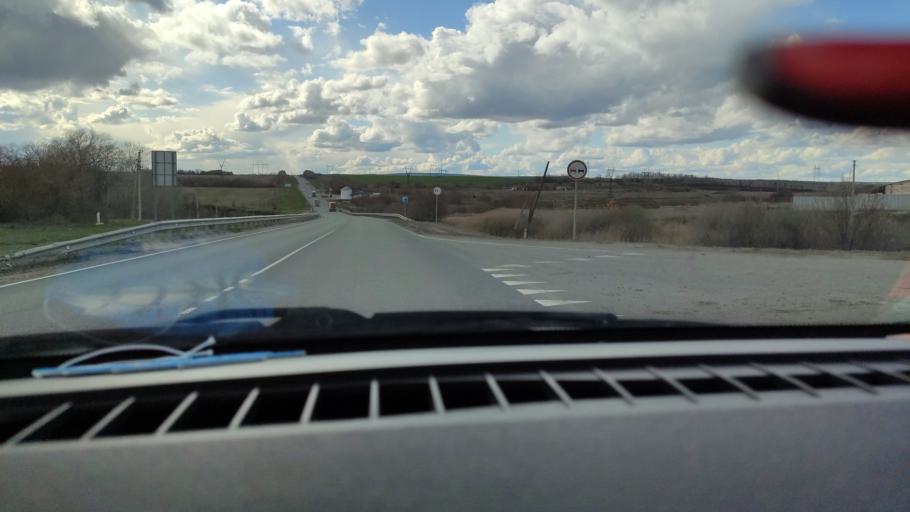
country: RU
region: Saratov
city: Tersa
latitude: 52.0983
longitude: 47.5266
